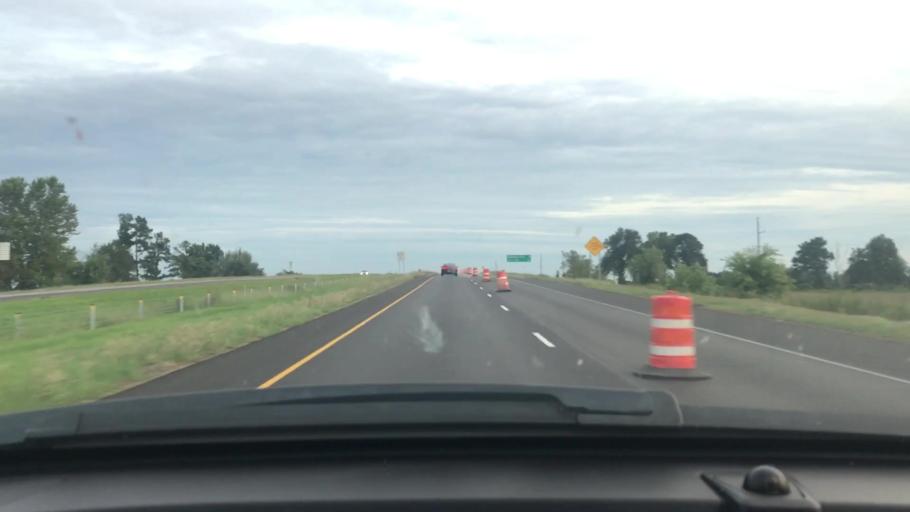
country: US
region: Arkansas
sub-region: Poinsett County
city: Trumann
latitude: 35.6229
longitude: -90.4968
